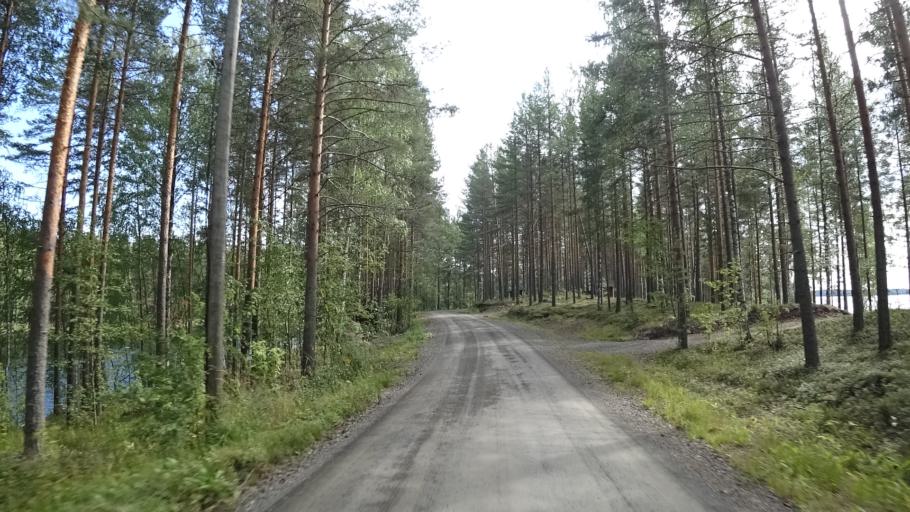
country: FI
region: North Karelia
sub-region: Joensuu
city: Pyhaeselkae
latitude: 62.3821
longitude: 29.8062
